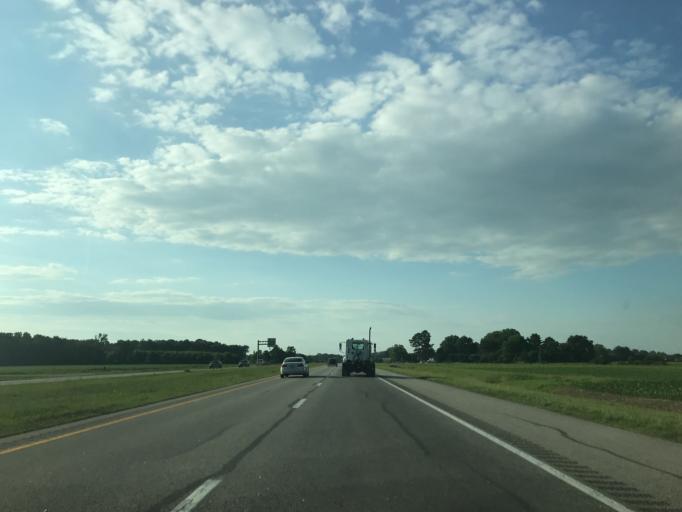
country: US
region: Maryland
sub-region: Caroline County
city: Denton
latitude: 38.8601
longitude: -75.8219
